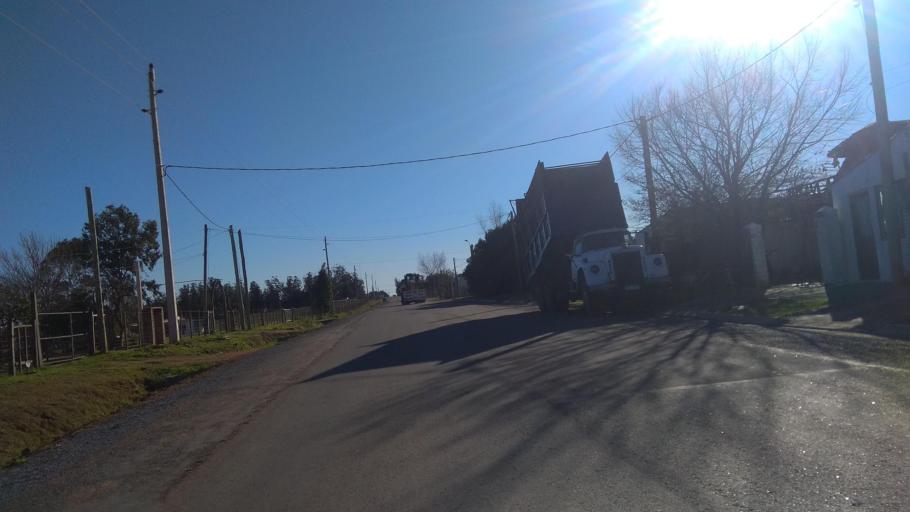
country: UY
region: Florida
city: Florida
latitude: -34.0996
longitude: -56.2414
